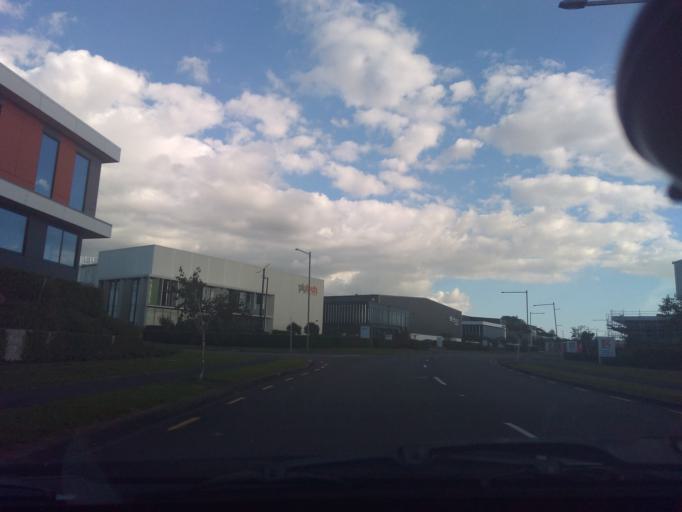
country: NZ
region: Auckland
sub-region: Auckland
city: Tamaki
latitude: -36.9331
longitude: 174.8766
